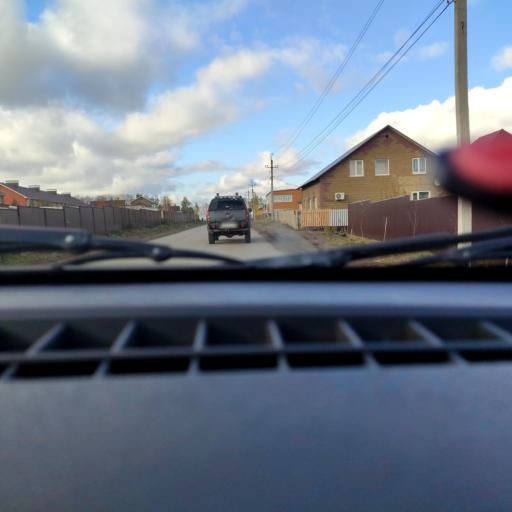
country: RU
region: Bashkortostan
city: Ufa
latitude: 54.6003
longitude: 55.9220
